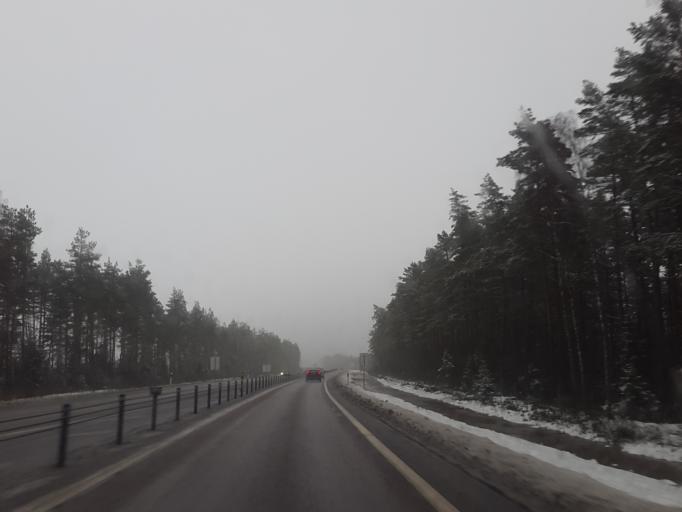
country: SE
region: Joenkoeping
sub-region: Jonkopings Kommun
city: Taberg
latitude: 57.7630
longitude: 14.0133
